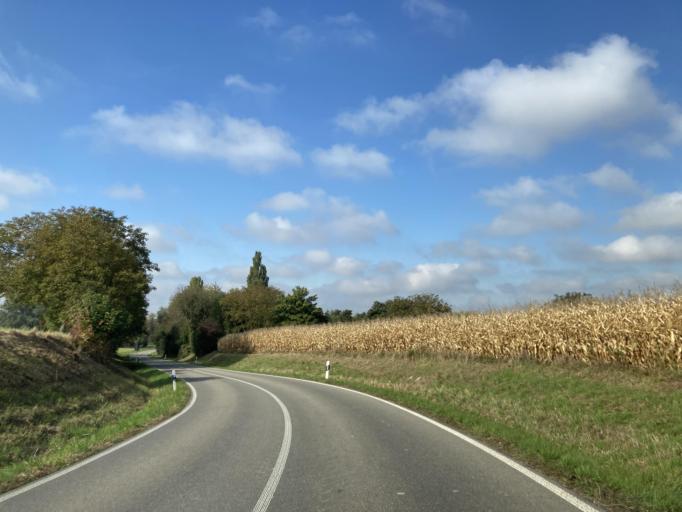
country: DE
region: Baden-Wuerttemberg
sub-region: Freiburg Region
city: Buggingen
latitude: 47.8377
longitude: 7.6585
